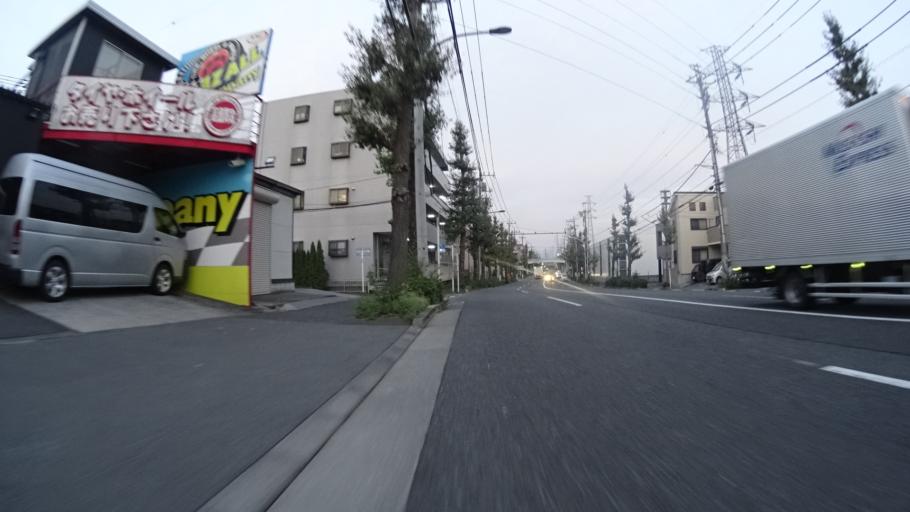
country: JP
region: Tokyo
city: Hino
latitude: 35.6886
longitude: 139.4033
